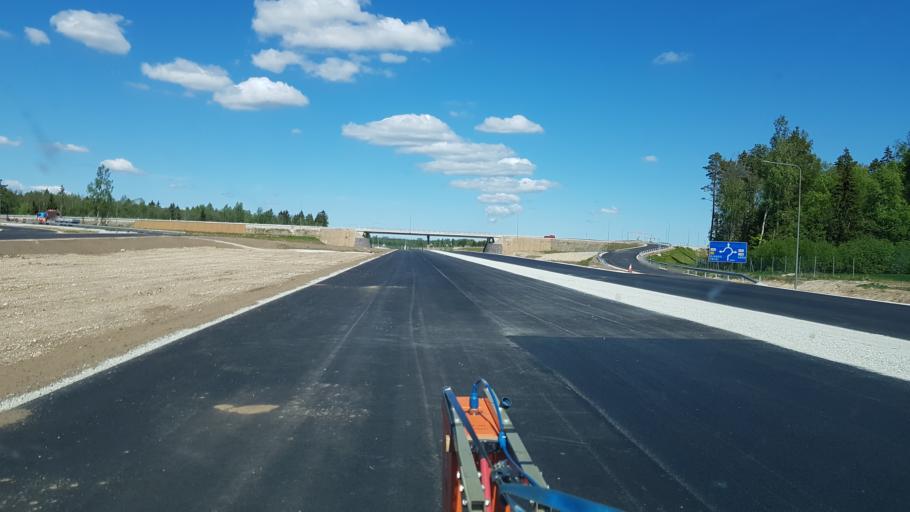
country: EE
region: Harju
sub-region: Anija vald
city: Kehra
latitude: 59.1030
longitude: 25.3149
